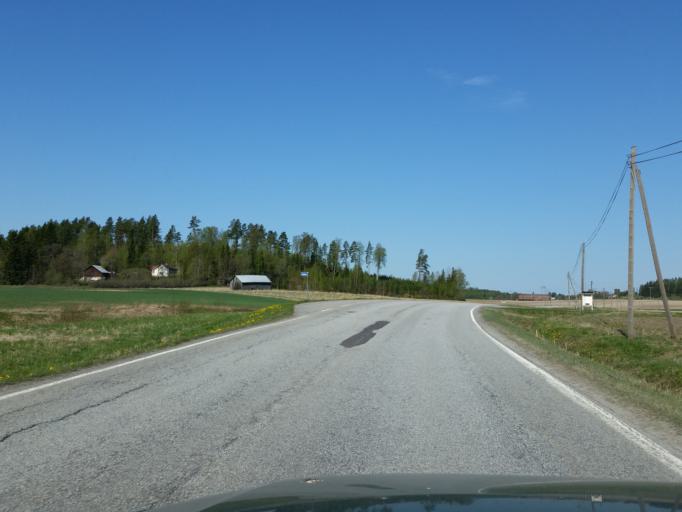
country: FI
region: Uusimaa
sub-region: Helsinki
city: Lohja
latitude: 60.1779
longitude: 24.0500
